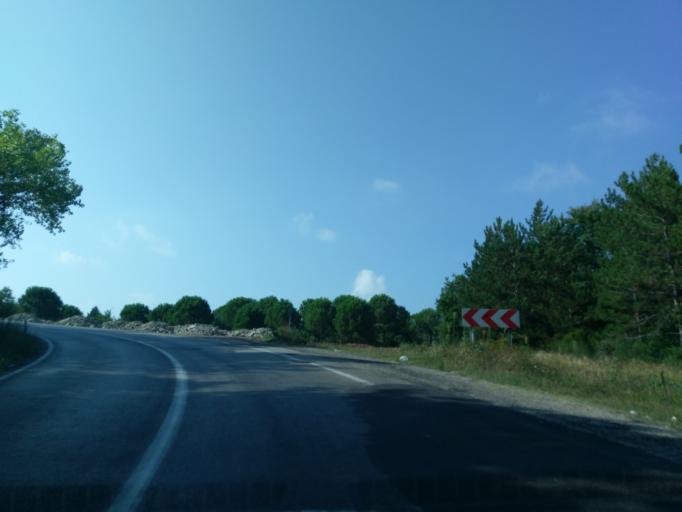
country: TR
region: Sinop
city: Yenikonak
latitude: 41.9417
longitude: 34.7137
